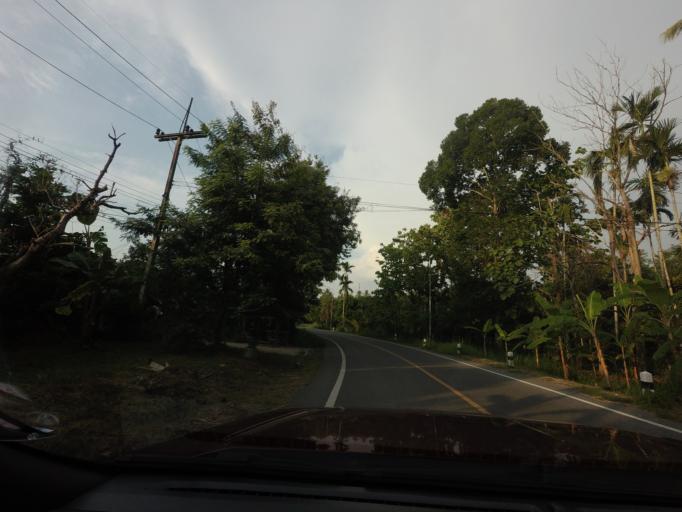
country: TH
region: Pattani
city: Khok Pho
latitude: 6.6703
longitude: 101.1042
